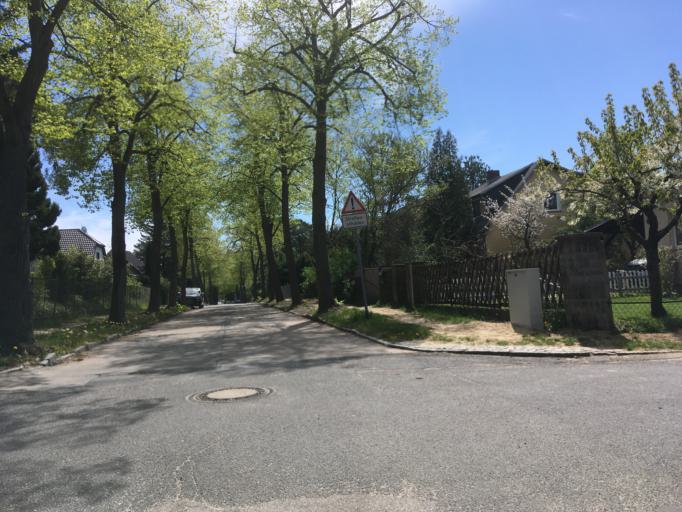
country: DE
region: Brandenburg
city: Zeuthen
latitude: 52.3452
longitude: 13.6073
